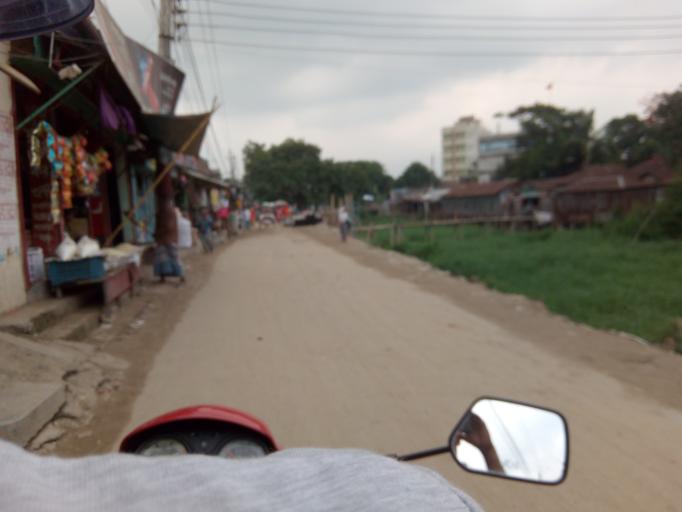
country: BD
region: Dhaka
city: Paltan
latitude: 23.7480
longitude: 90.4459
